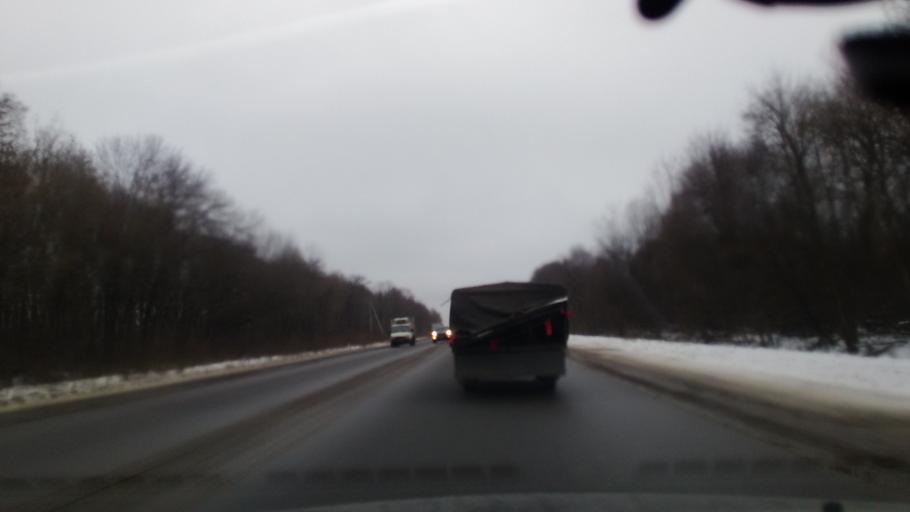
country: RU
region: Tula
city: Tula
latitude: 54.1420
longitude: 37.6614
